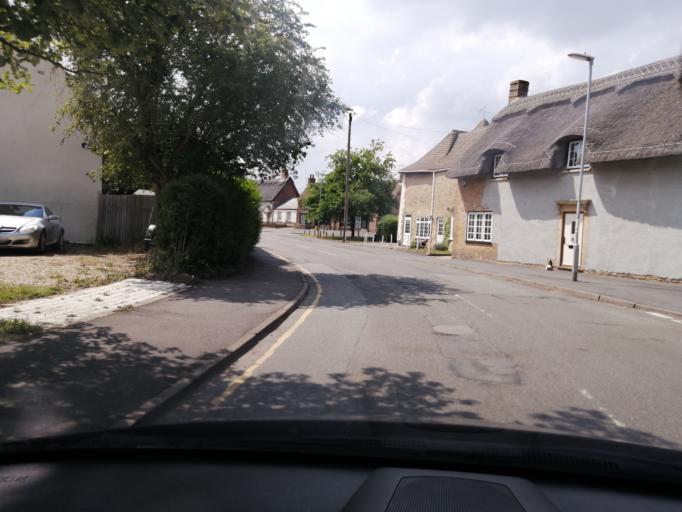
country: GB
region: England
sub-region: Cambridgeshire
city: Yaxley
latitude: 52.5141
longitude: -0.2570
